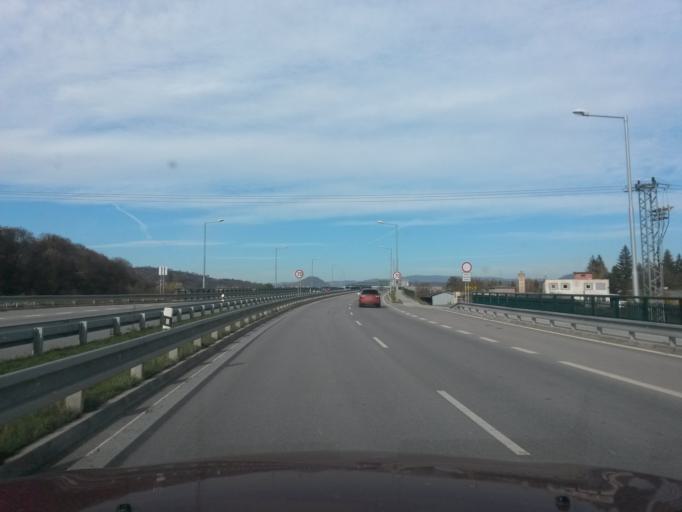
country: SK
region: Presovsky
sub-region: Okres Presov
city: Presov
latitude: 48.9778
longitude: 21.2413
